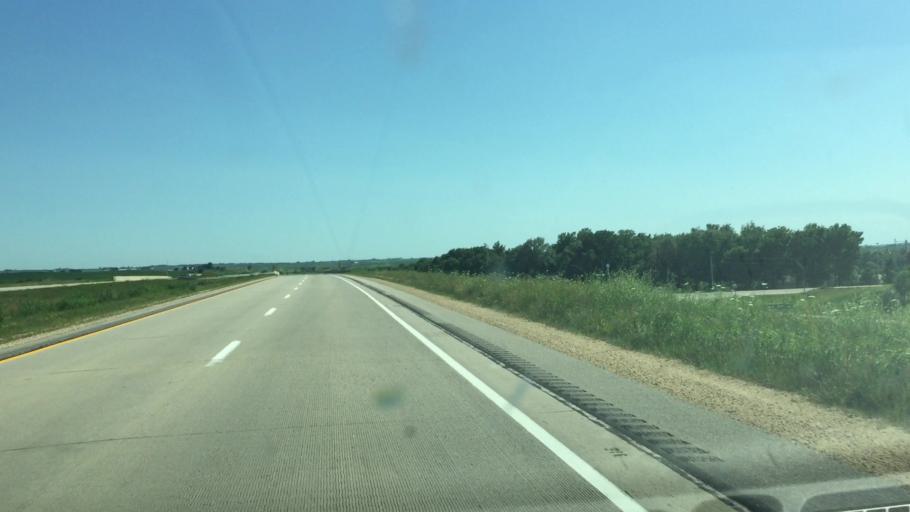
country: US
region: Iowa
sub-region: Jones County
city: Monticello
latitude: 42.2325
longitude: -91.1709
